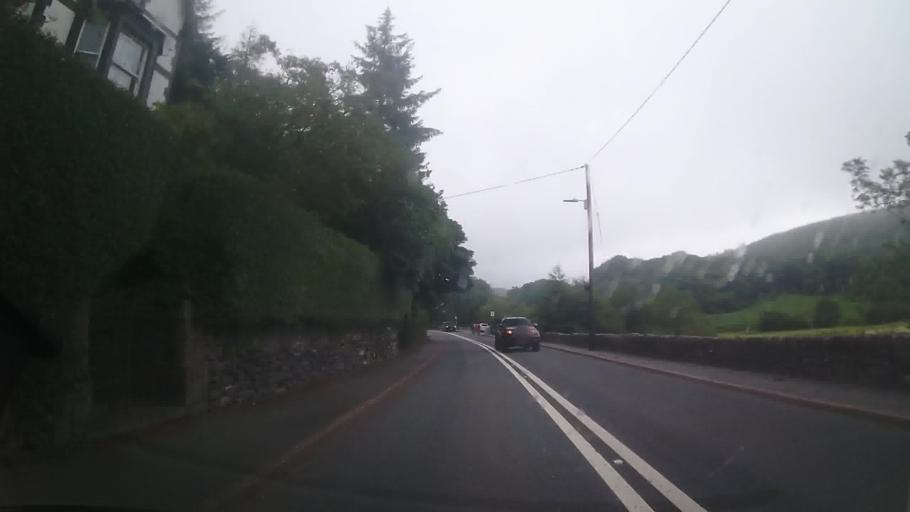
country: GB
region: Wales
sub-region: Conwy
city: Betws-y-Coed
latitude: 53.1028
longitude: -3.9090
